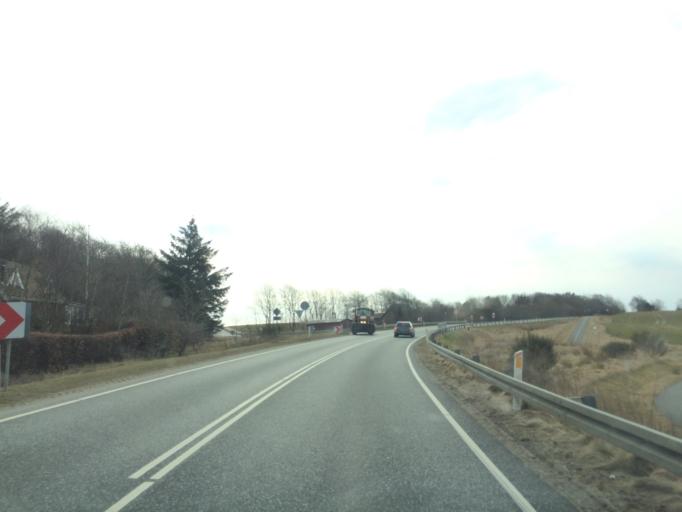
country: DK
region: Central Jutland
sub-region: Ringkobing-Skjern Kommune
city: Videbaek
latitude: 56.1078
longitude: 8.5070
